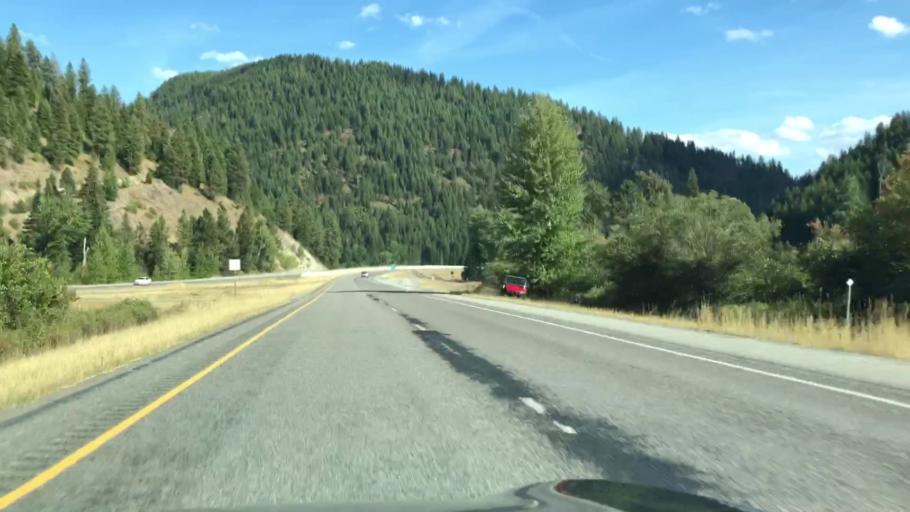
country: US
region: Montana
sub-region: Sanders County
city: Thompson Falls
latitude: 47.3564
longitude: -115.2995
